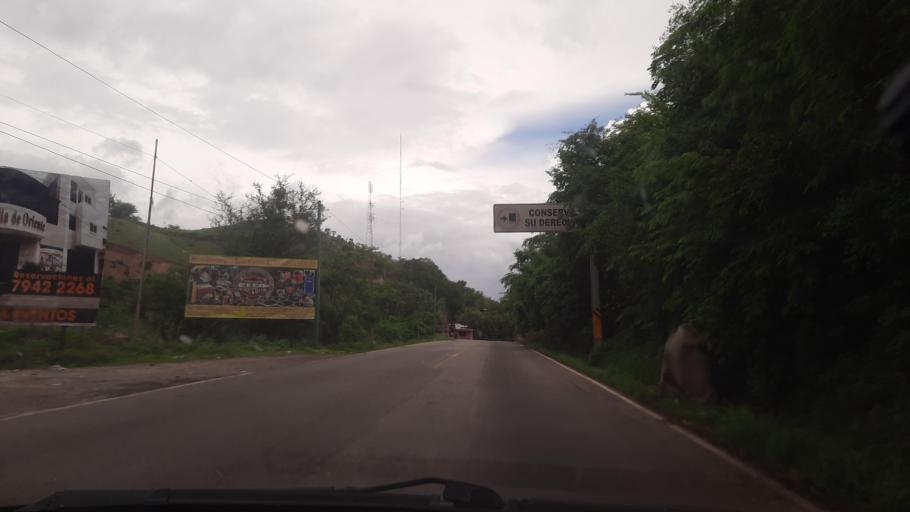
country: GT
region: Chiquimula
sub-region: Municipio de Chiquimula
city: Chiquimula
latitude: 14.8650
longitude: -89.5094
